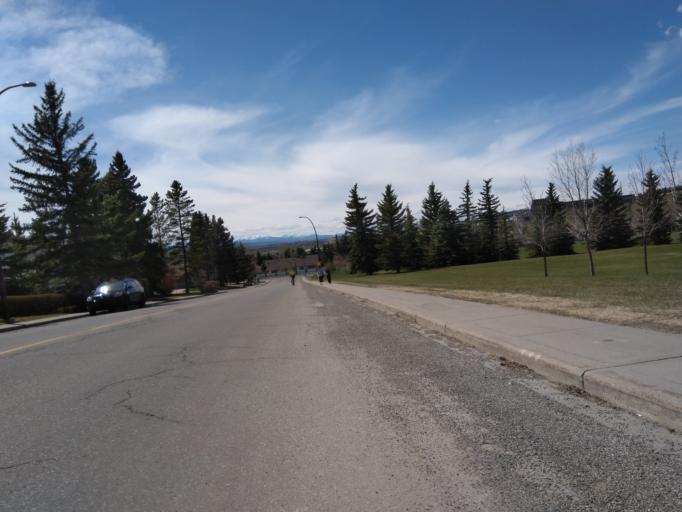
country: CA
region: Alberta
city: Calgary
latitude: 51.0125
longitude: -114.1566
